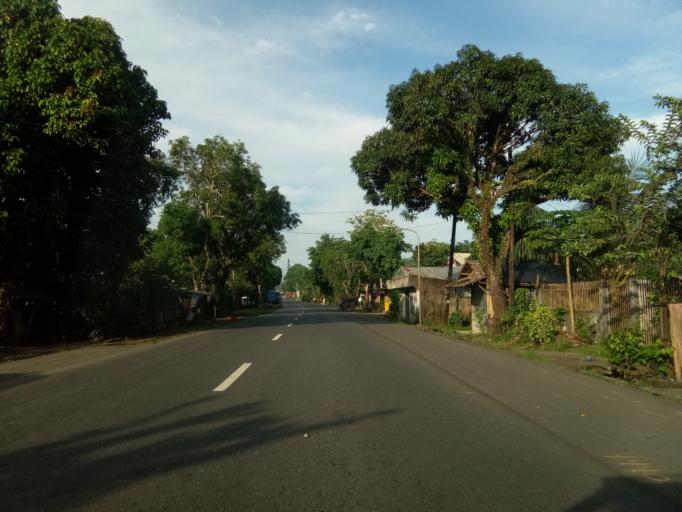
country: PH
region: Caraga
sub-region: Province of Surigao del Norte
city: Tubod
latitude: 9.5398
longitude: 125.5648
